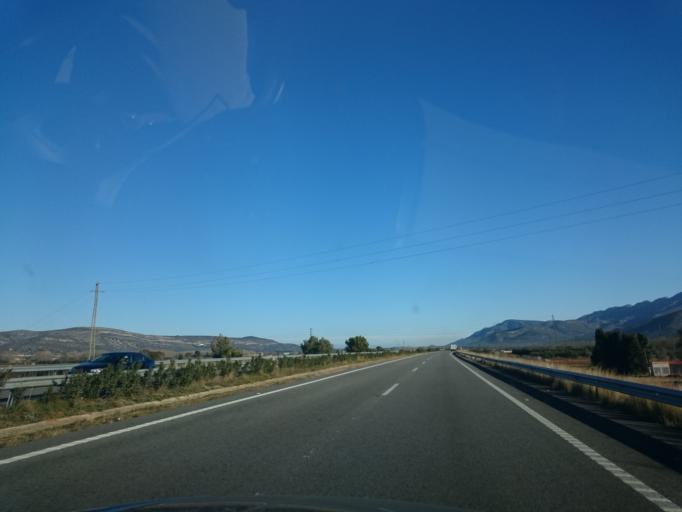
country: ES
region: Catalonia
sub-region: Provincia de Tarragona
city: Ulldecona
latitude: 40.5843
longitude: 0.4574
